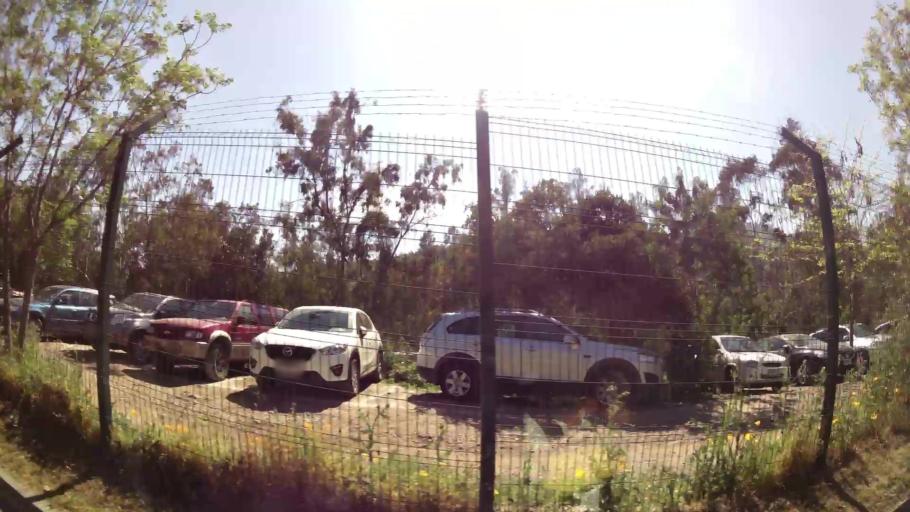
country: CL
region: Santiago Metropolitan
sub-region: Provincia de Santiago
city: Villa Presidente Frei, Nunoa, Santiago, Chile
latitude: -33.4327
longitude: -70.5208
